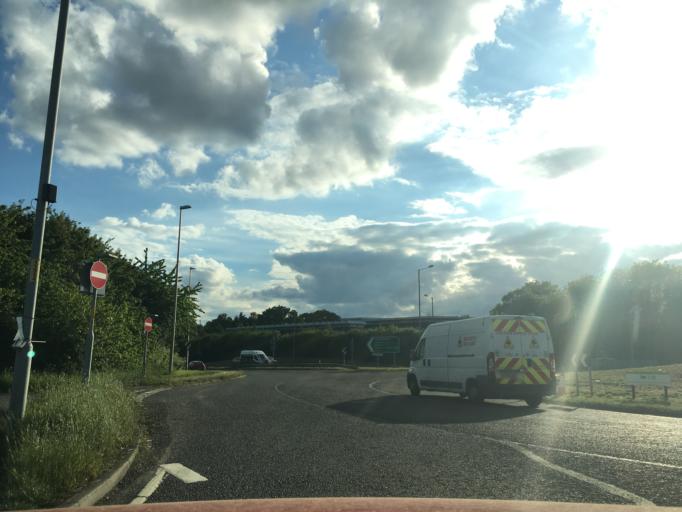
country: GB
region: England
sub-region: Worcestershire
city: Worcester
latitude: 52.1859
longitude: -2.1746
